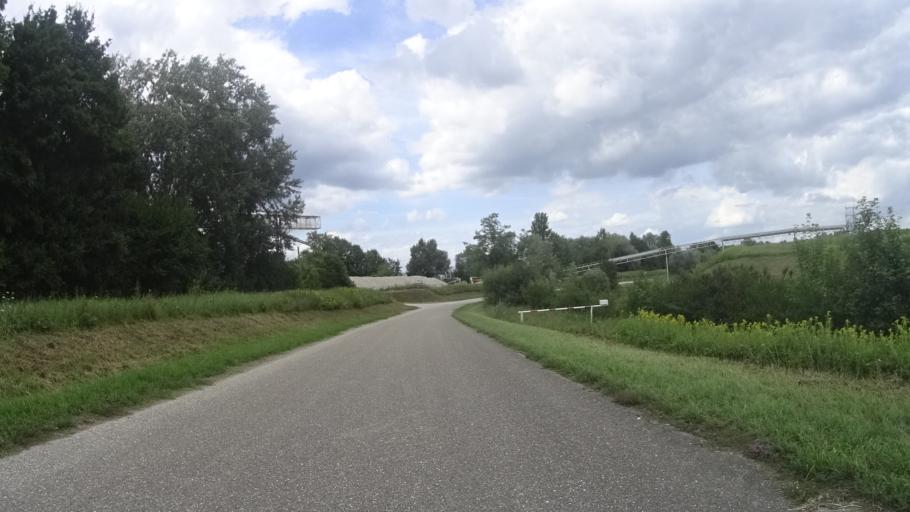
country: DE
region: Baden-Wuerttemberg
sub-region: Karlsruhe Region
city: Rheinmuenster
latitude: 48.7889
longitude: 8.0283
